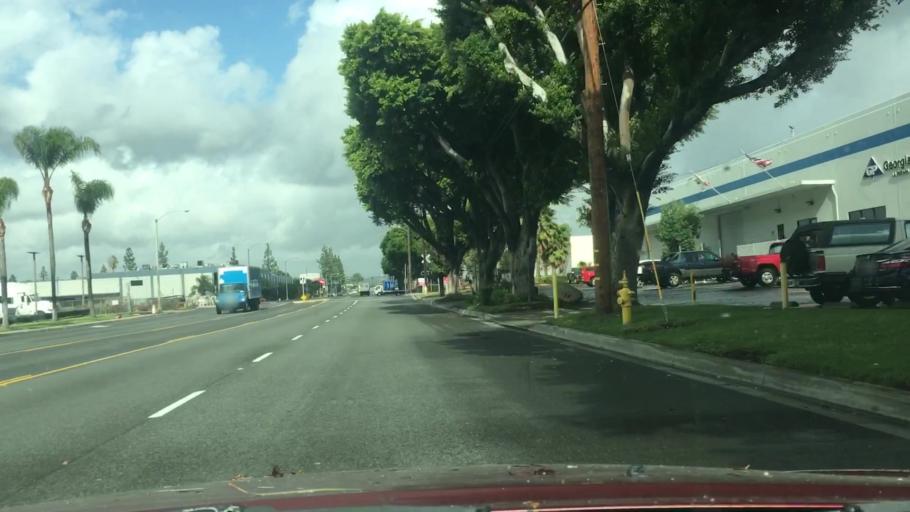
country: US
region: California
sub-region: Los Angeles County
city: La Mirada
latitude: 33.8907
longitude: -118.0289
